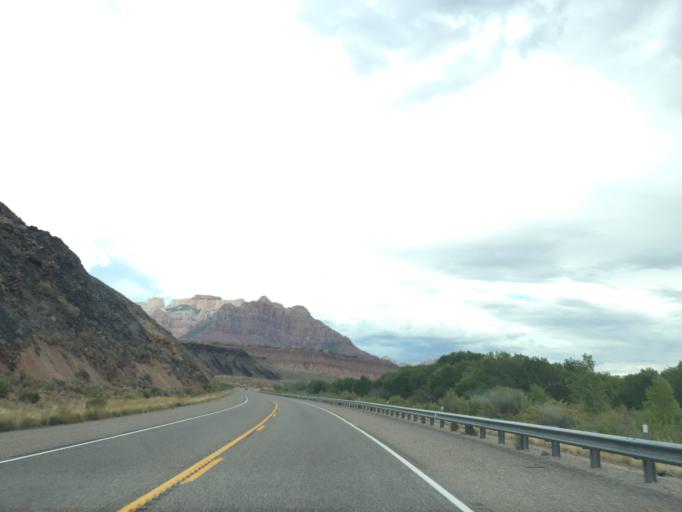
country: US
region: Utah
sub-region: Washington County
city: LaVerkin
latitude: 37.1684
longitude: -113.0994
